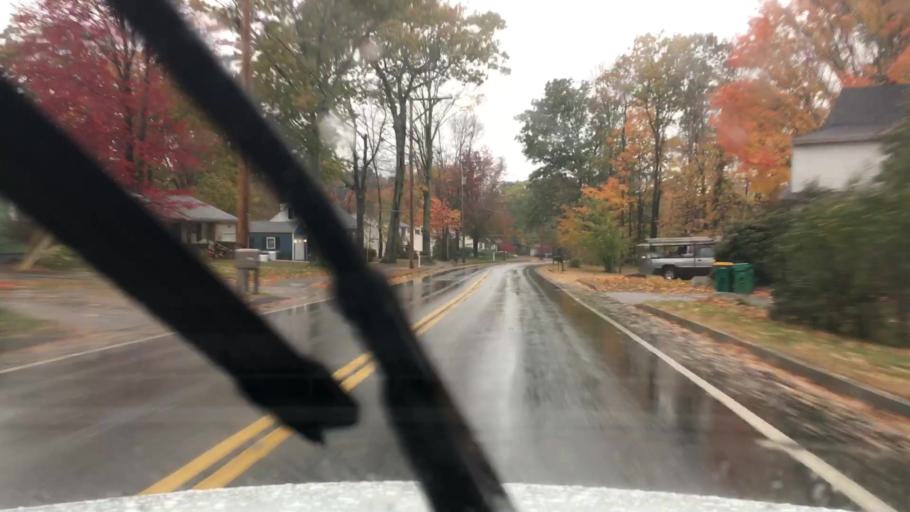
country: US
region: New Hampshire
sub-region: Strafford County
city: Rochester
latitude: 43.3241
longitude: -70.9526
